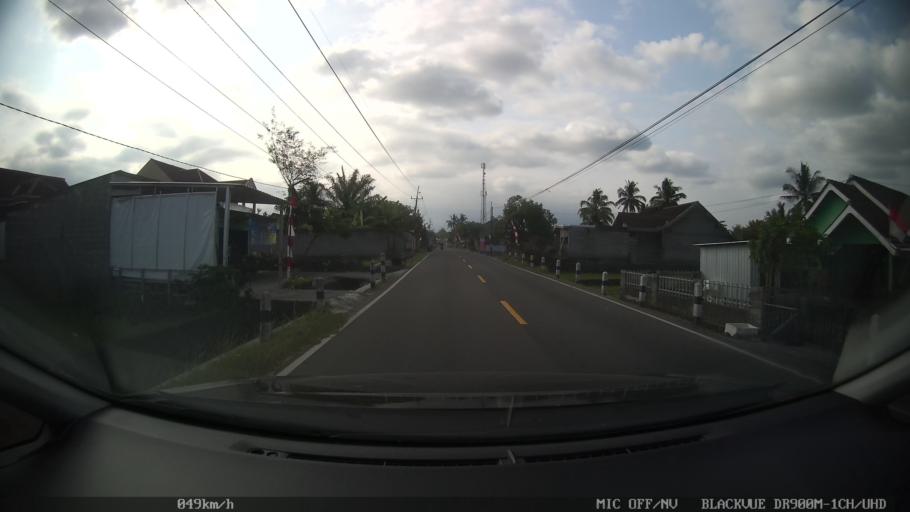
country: ID
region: Central Java
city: Candi Prambanan
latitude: -7.7023
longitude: 110.4666
